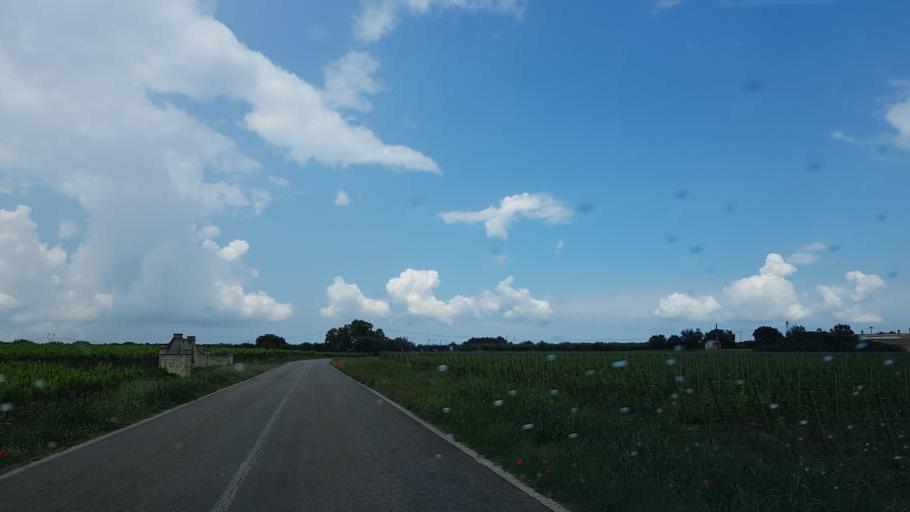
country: IT
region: Apulia
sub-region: Provincia di Brindisi
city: San Donaci
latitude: 40.4720
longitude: 17.9326
